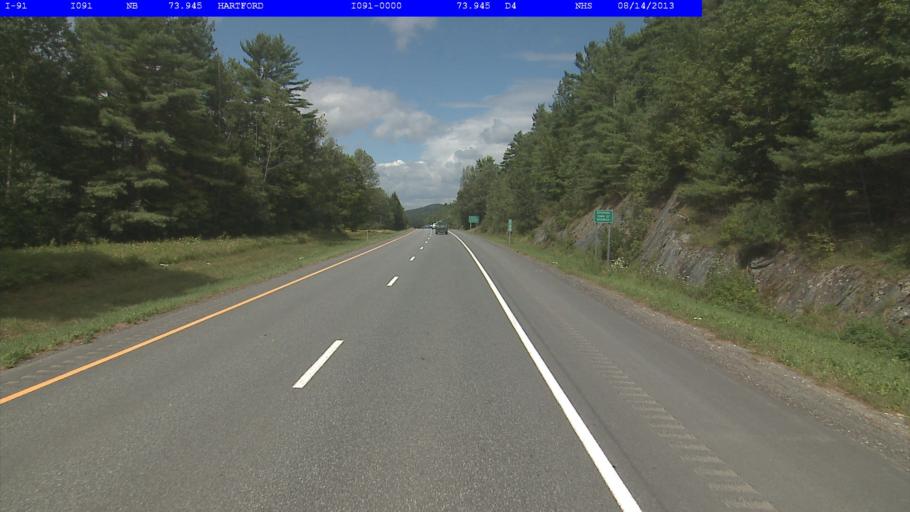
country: US
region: Vermont
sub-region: Windsor County
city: Wilder
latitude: 43.6935
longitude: -72.3106
